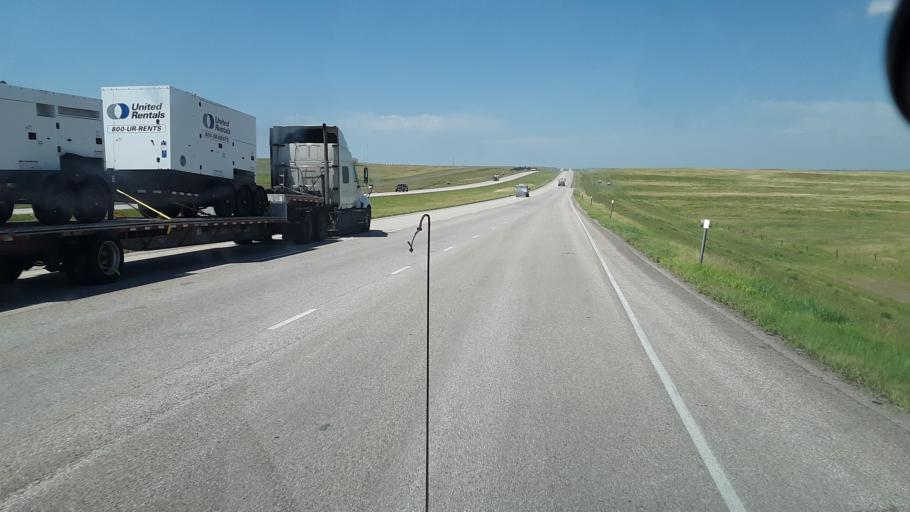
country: US
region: South Dakota
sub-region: Haakon County
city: Philip
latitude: 43.8365
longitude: -101.7800
